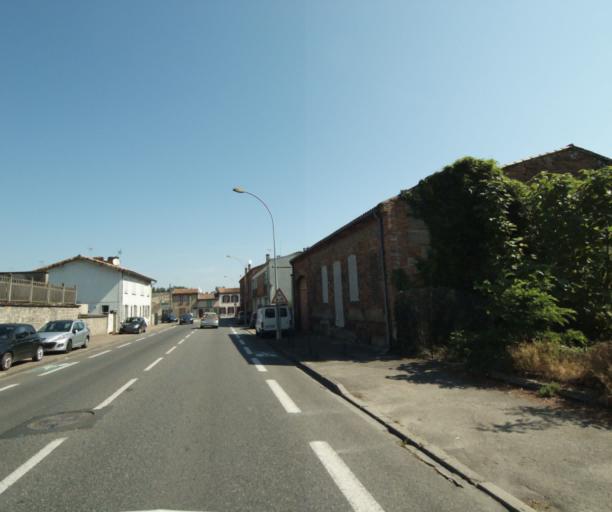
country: FR
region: Midi-Pyrenees
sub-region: Departement du Tarn-et-Garonne
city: Montauban
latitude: 44.0160
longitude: 1.3414
